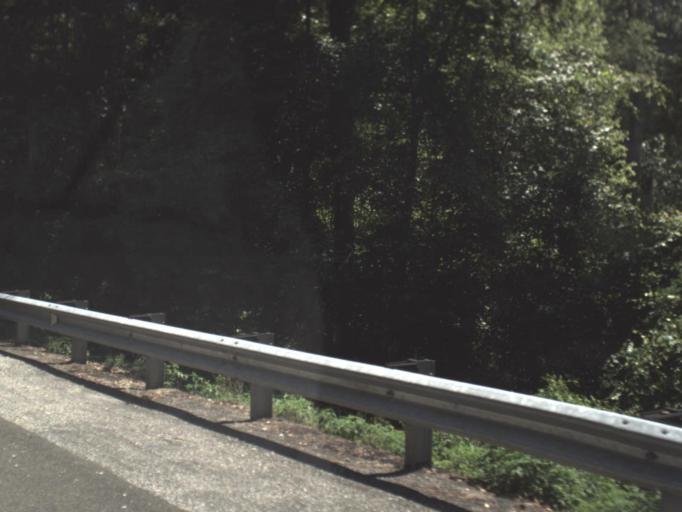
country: US
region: Florida
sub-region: Clay County
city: Green Cove Springs
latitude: 30.0423
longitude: -81.6668
